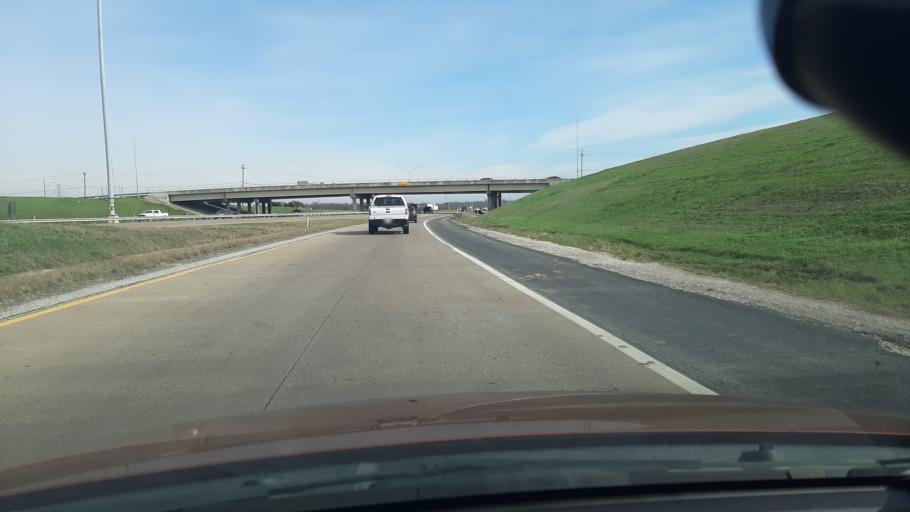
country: US
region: Texas
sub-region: Tarrant County
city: Benbrook
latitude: 32.6835
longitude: -97.4543
